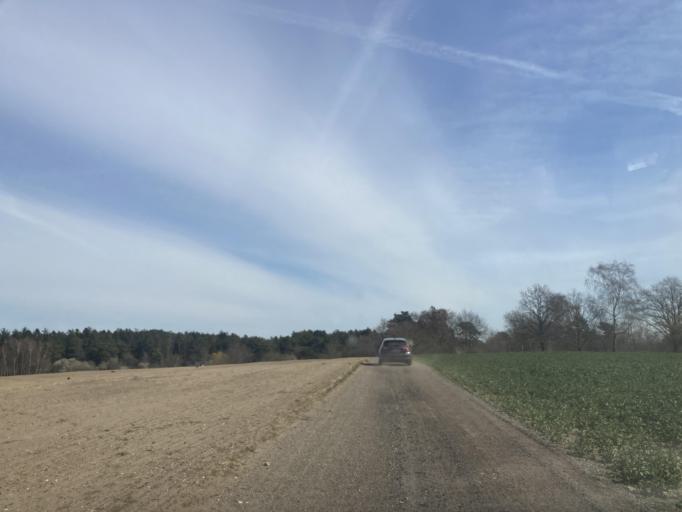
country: DK
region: Capital Region
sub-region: Helsingor Kommune
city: Hornbaek
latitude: 56.0789
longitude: 12.4018
